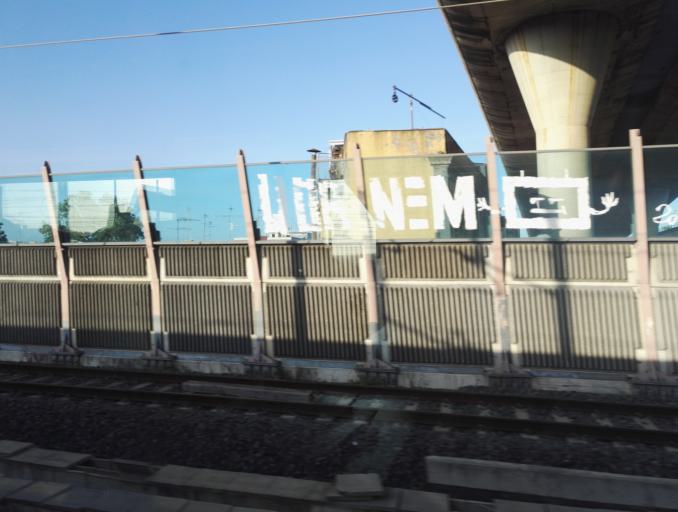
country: IT
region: Campania
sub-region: Provincia di Napoli
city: Arpino
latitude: 40.8644
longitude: 14.2957
